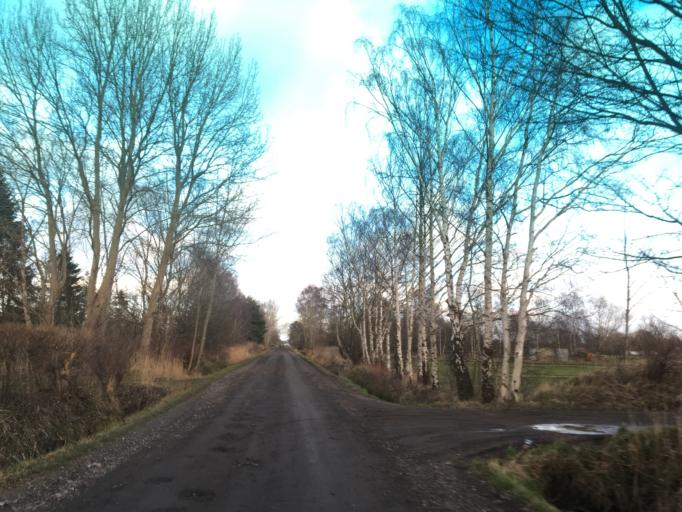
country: DK
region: Capital Region
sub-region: Tarnby Kommune
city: Tarnby
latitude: 55.5834
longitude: 12.5825
